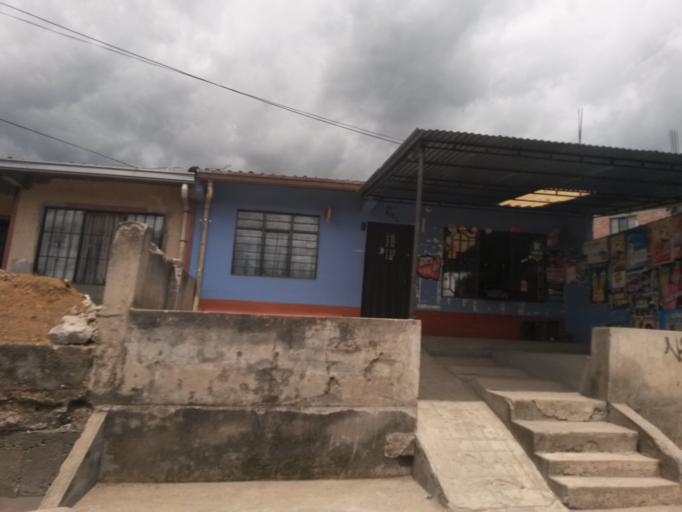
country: CO
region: Cauca
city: Popayan
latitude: 2.4532
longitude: -76.6313
